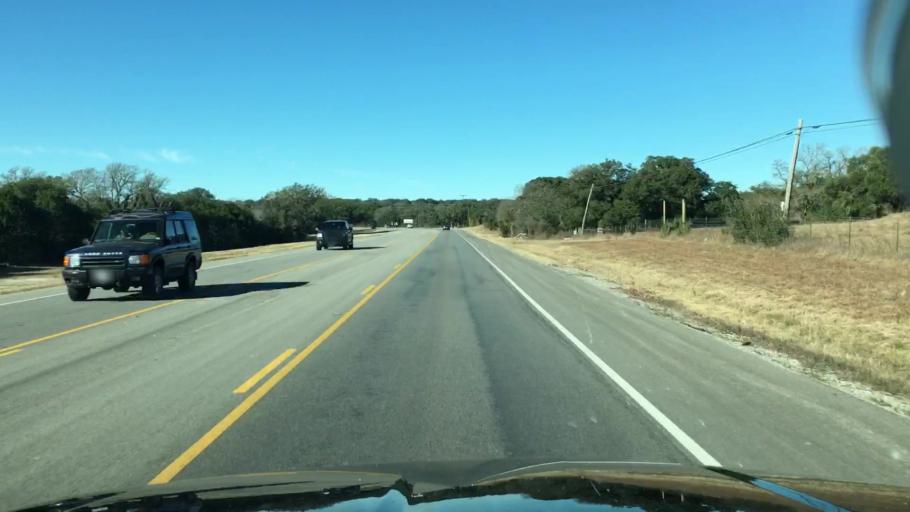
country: US
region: Texas
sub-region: Hays County
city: Dripping Springs
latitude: 30.2006
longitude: -98.1932
